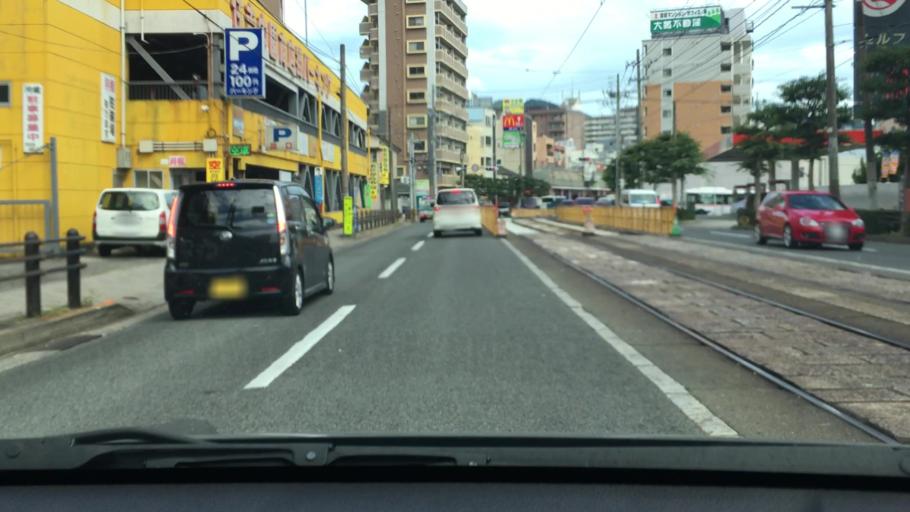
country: JP
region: Nagasaki
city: Obita
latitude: 32.7933
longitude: 129.8586
